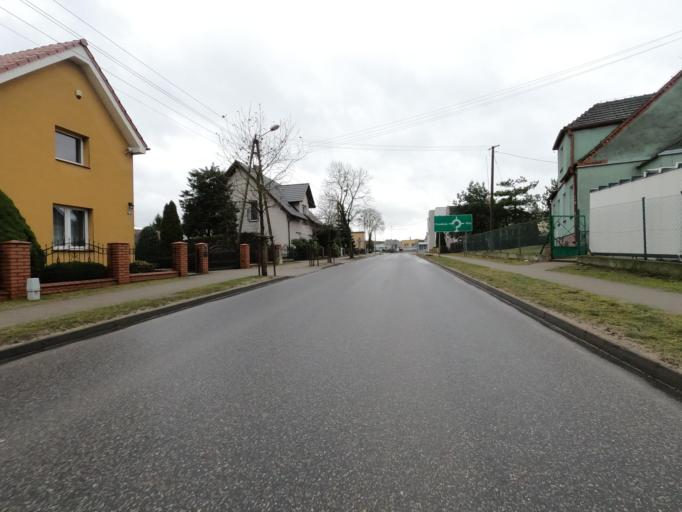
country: PL
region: Greater Poland Voivodeship
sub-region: Powiat pilski
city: Kaczory
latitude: 53.1046
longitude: 16.8816
